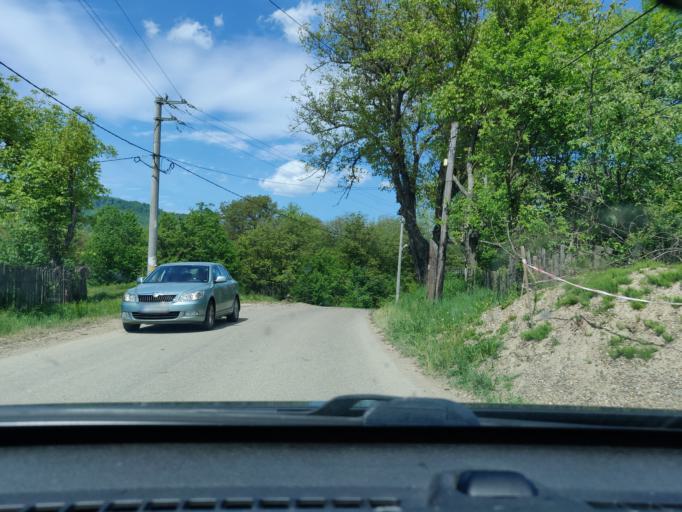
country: RO
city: Vizantea-Manastireasca
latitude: 45.9796
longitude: 26.7996
